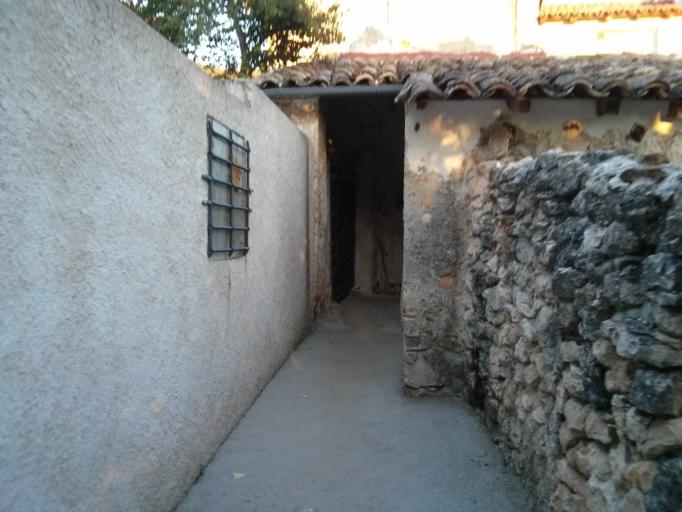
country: ES
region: Castille-La Mancha
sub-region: Provincia de Guadalajara
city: Mantiel
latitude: 40.6224
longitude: -2.6363
